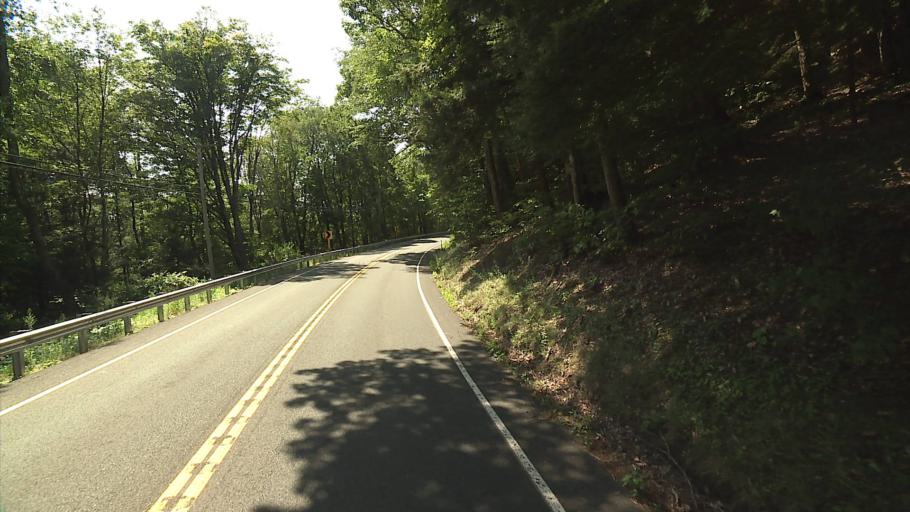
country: US
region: Massachusetts
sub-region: Berkshire County
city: New Marlborough
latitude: 42.0030
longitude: -73.2033
